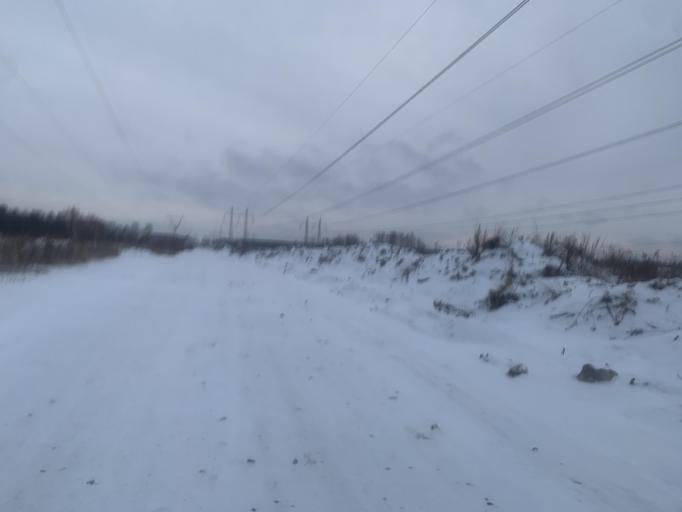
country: RU
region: Chelyabinsk
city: Roshchino
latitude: 55.1915
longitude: 61.2592
